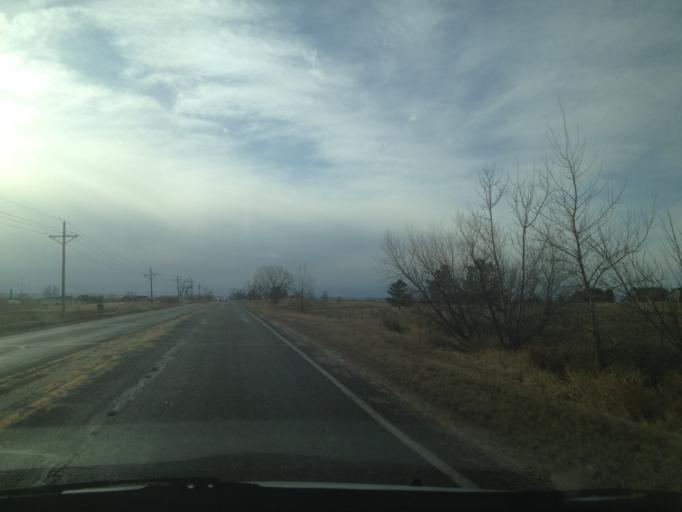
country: US
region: Colorado
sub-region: Weld County
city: Fort Lupton
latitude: 40.0803
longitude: -104.7851
